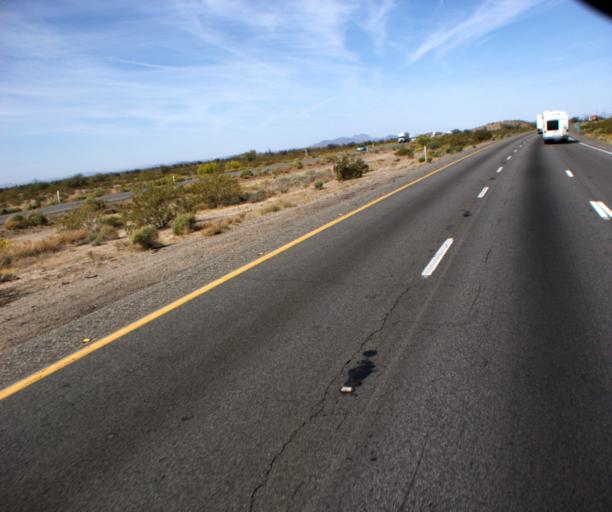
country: US
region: Arizona
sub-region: Maricopa County
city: Buckeye
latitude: 33.4296
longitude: -112.6339
